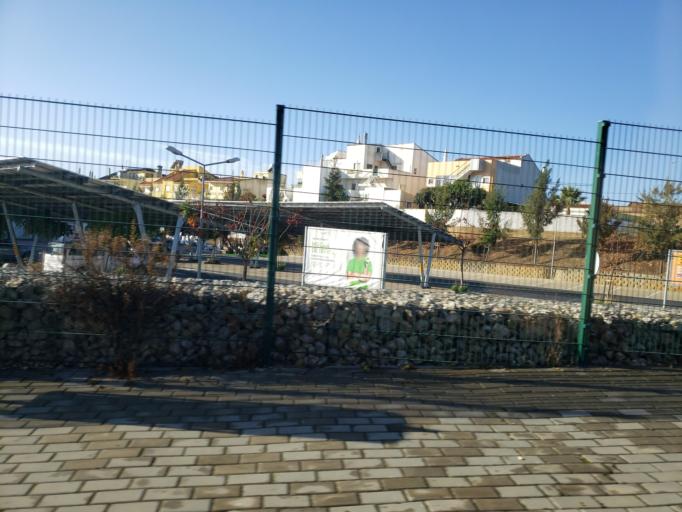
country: PT
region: Faro
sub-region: Portimao
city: Portimao
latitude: 37.1486
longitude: -8.5505
